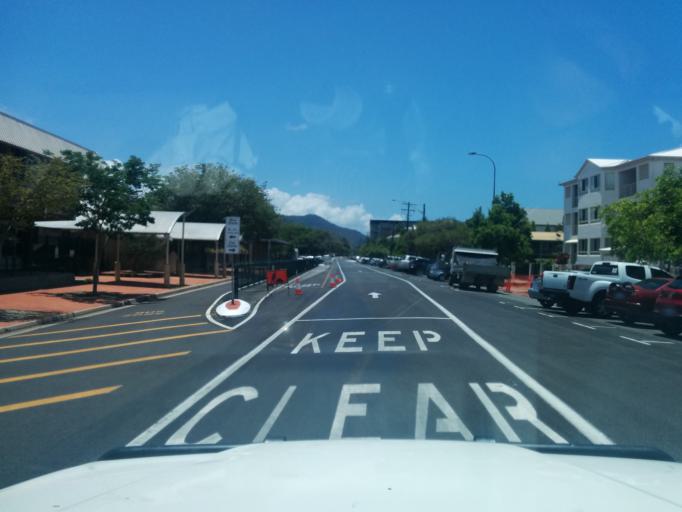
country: AU
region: Queensland
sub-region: Cairns
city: Cairns
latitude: -16.9158
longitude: 145.7687
